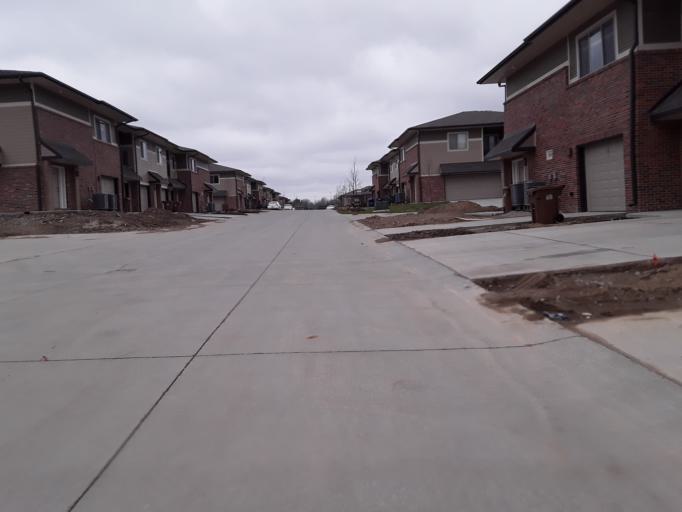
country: US
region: Nebraska
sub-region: Lancaster County
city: Lincoln
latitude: 40.8505
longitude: -96.6006
